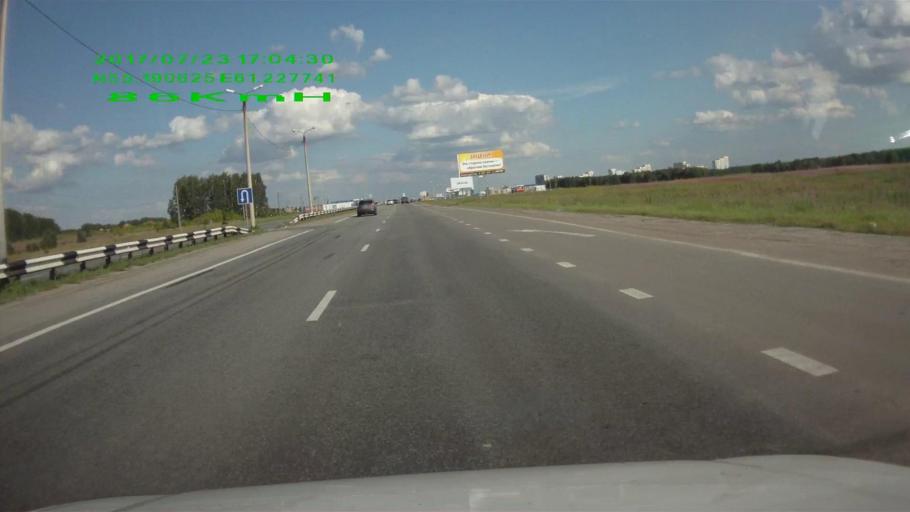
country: RU
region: Chelyabinsk
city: Roshchino
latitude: 55.1902
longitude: 61.2293
